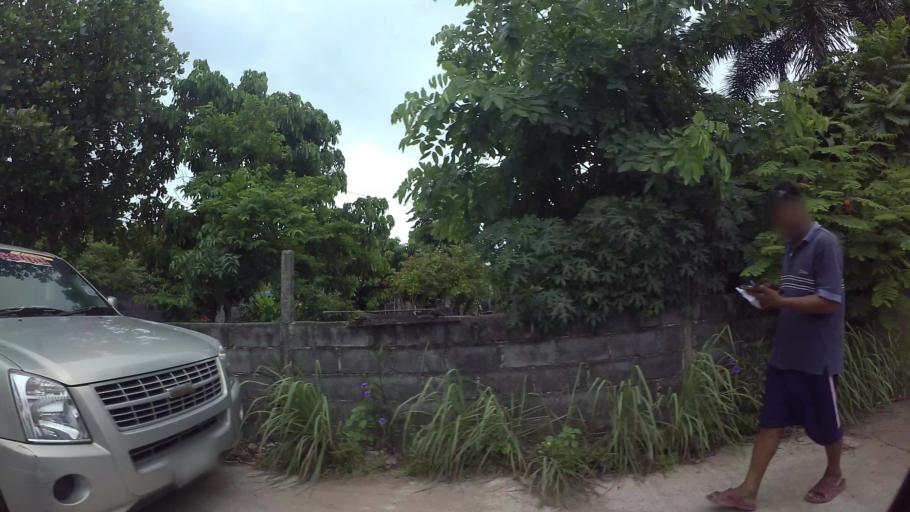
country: TH
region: Chon Buri
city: Si Racha
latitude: 13.1848
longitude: 100.9798
